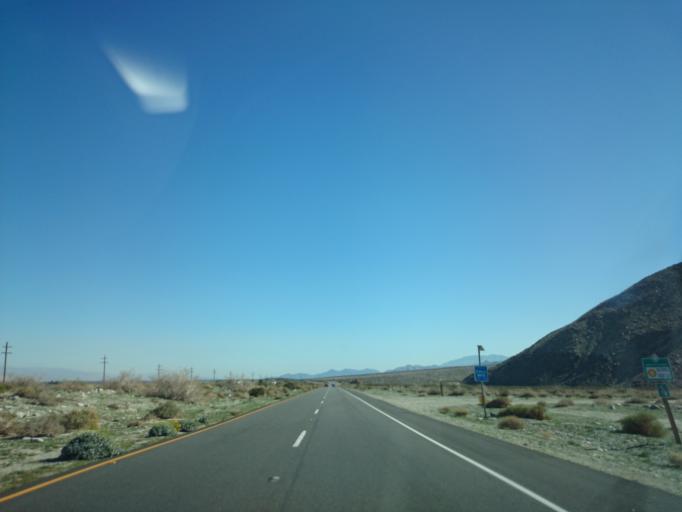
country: US
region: California
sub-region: Riverside County
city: Garnet
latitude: 33.8755
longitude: -116.5849
